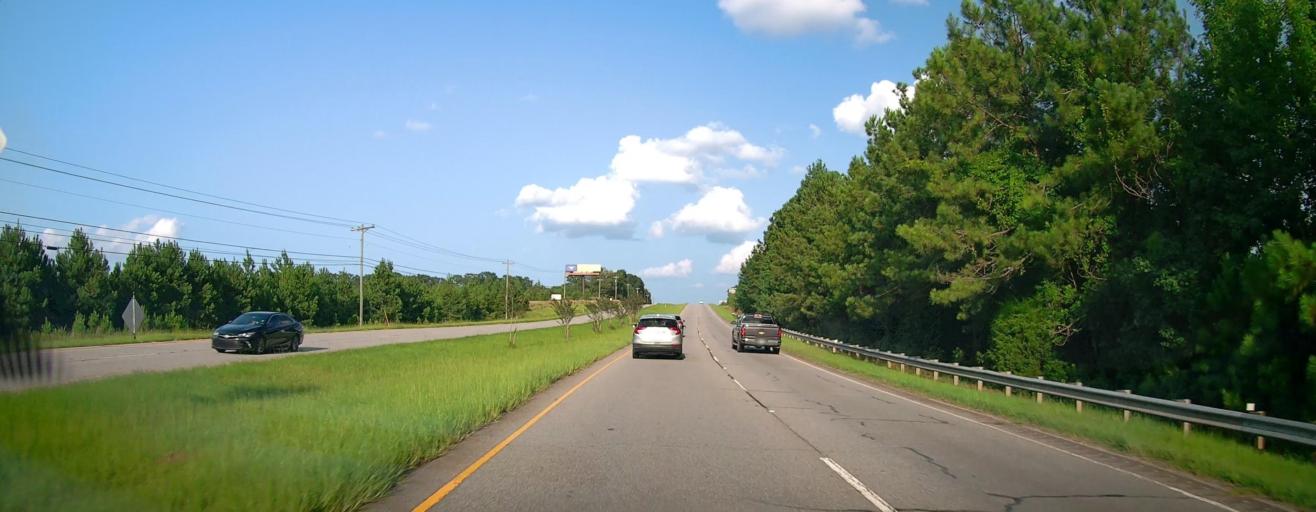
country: US
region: Georgia
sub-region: Houston County
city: Centerville
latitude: 32.6140
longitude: -83.7325
